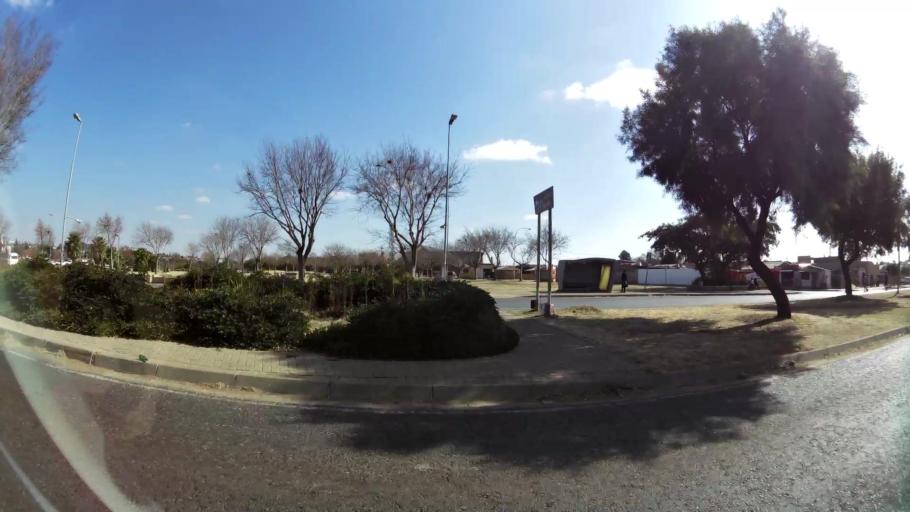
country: ZA
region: Gauteng
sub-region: City of Johannesburg Metropolitan Municipality
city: Soweto
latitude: -26.2627
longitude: 27.8850
